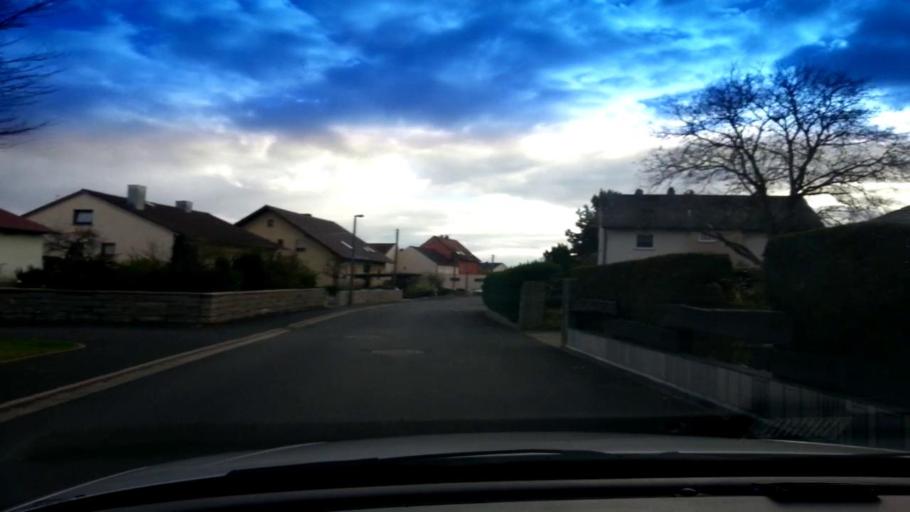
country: DE
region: Bavaria
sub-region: Upper Franconia
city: Rattelsdorf
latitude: 50.0091
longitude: 10.9027
